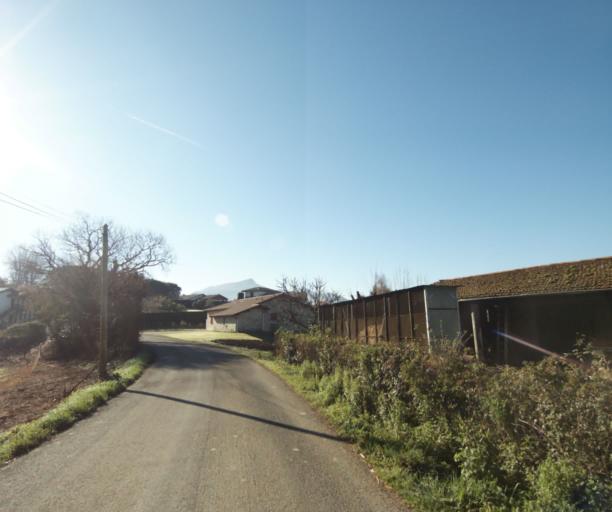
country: FR
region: Aquitaine
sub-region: Departement des Pyrenees-Atlantiques
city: Ciboure
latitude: 43.3677
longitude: -1.6648
